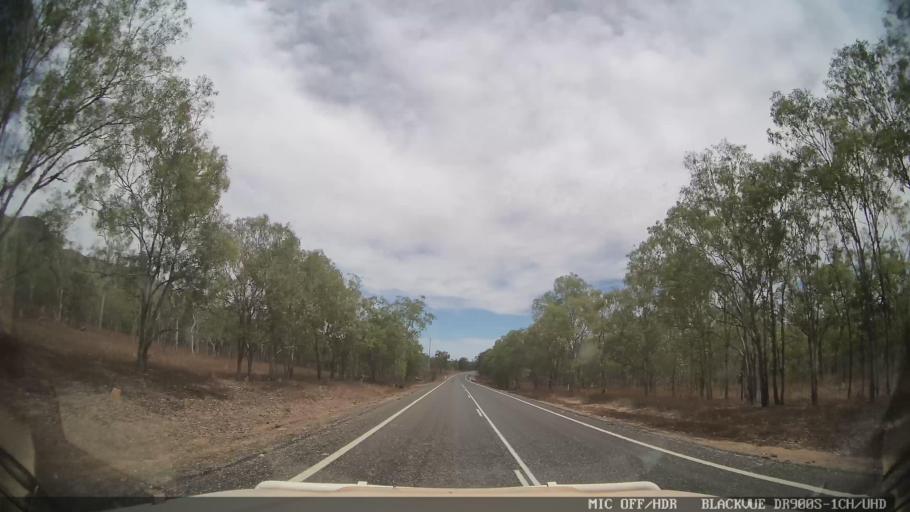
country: AU
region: Queensland
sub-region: Cairns
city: Port Douglas
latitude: -16.2485
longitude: 144.7264
